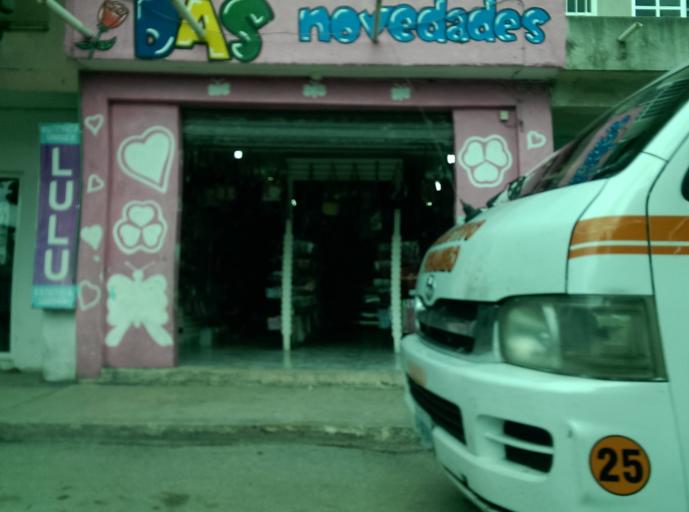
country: MX
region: Quintana Roo
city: Tulum
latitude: 20.2095
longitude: -87.4637
